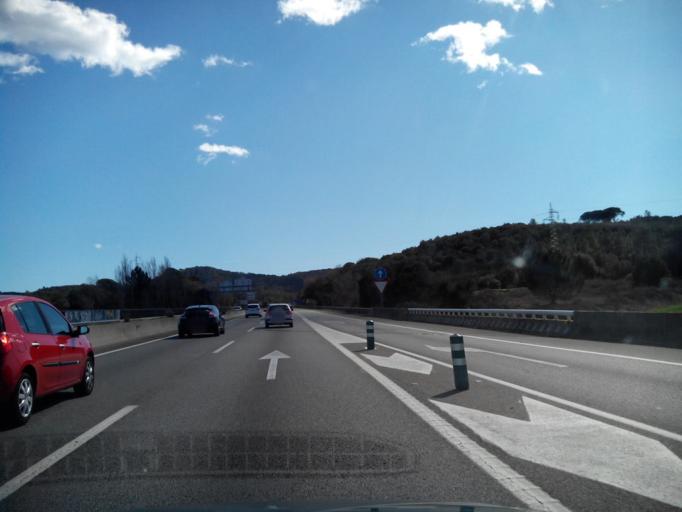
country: ES
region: Catalonia
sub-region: Provincia de Barcelona
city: La Roca del Valles
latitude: 41.5914
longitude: 2.3441
